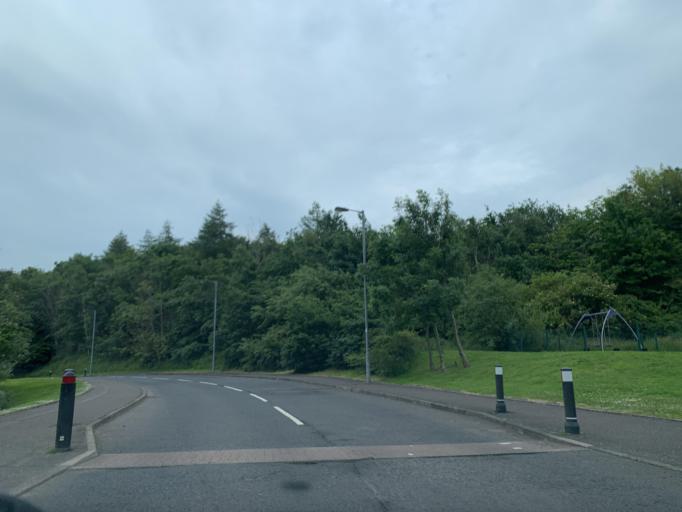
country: GB
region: Scotland
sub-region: East Renfrewshire
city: Newton Mearns
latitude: 55.7707
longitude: -4.3502
